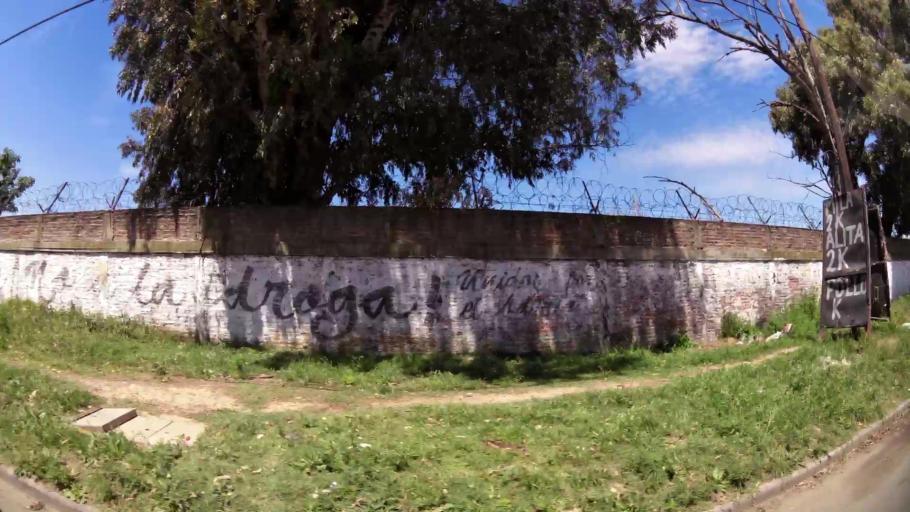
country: AR
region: Buenos Aires
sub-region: Partido de Quilmes
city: Quilmes
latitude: -34.7305
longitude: -58.3215
